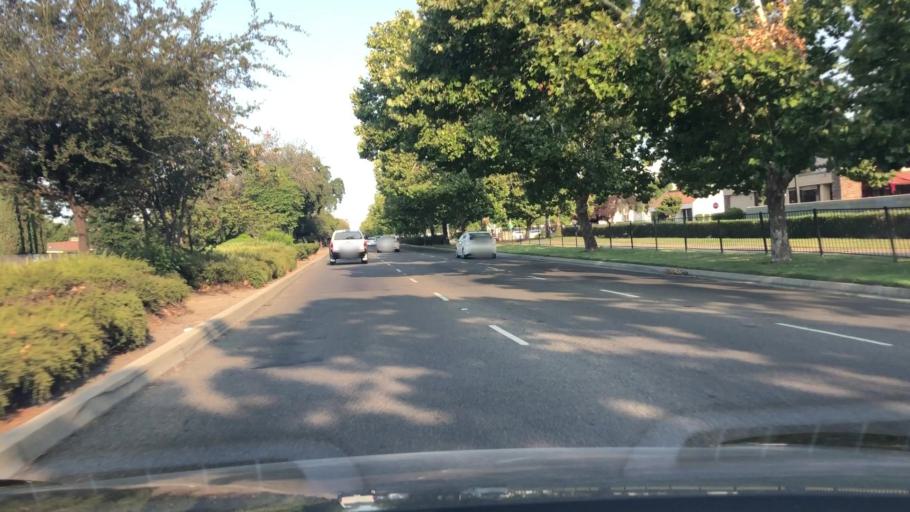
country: US
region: California
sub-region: Fresno County
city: Clovis
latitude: 36.8374
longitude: -119.7556
